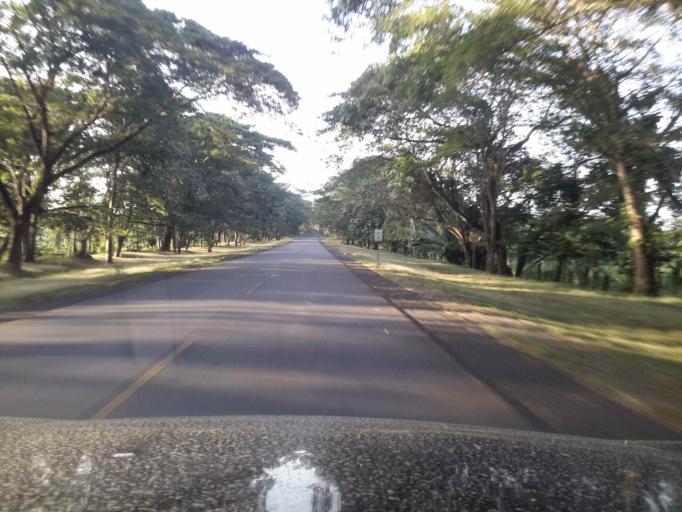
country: NI
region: Rio San Juan
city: San Miguelito
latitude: 11.4251
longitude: -84.8486
